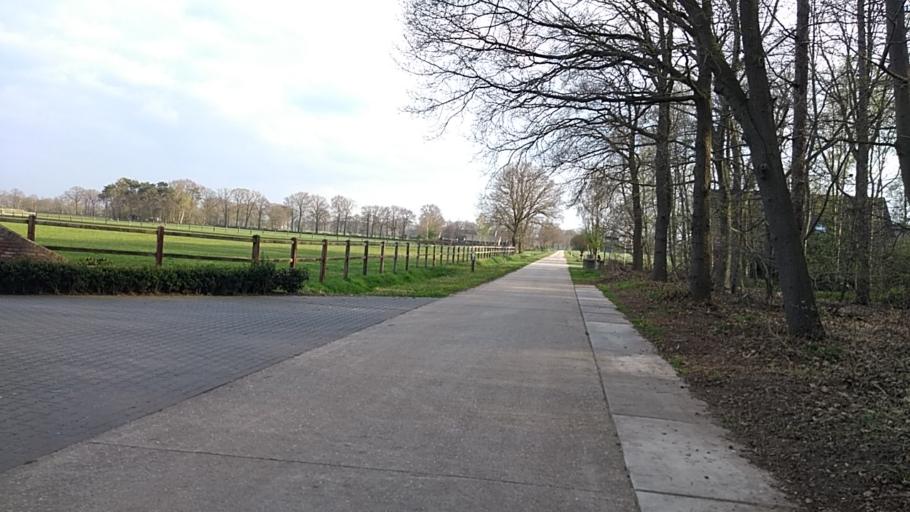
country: NL
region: Overijssel
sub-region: Gemeente Borne
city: Borne
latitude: 52.3505
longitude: 6.7272
